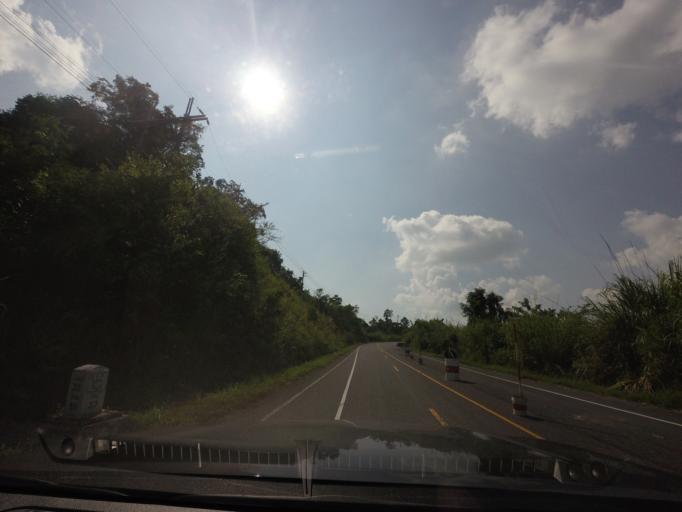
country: TH
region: Nan
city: Santi Suk
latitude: 18.9726
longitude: 101.0227
